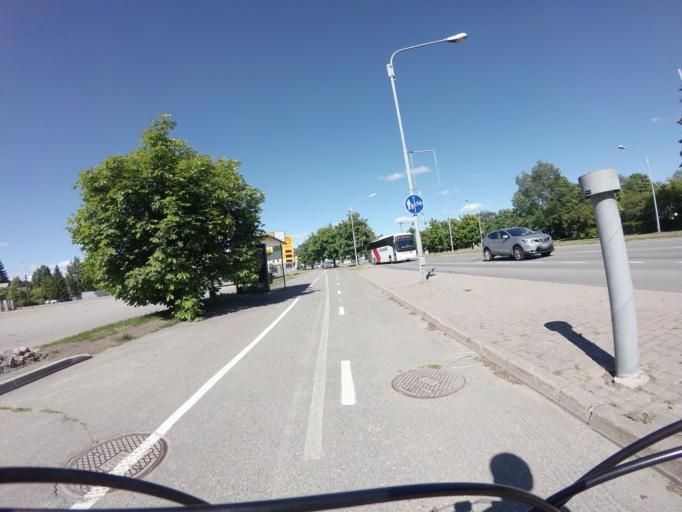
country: FI
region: Varsinais-Suomi
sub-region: Turku
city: Turku
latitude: 60.4635
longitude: 22.2698
